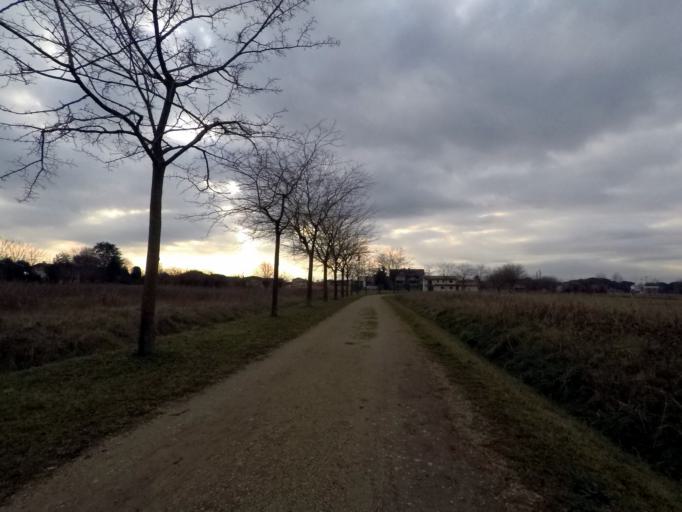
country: IT
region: Friuli Venezia Giulia
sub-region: Provincia di Udine
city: Colugna
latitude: 46.0972
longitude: 13.2015
